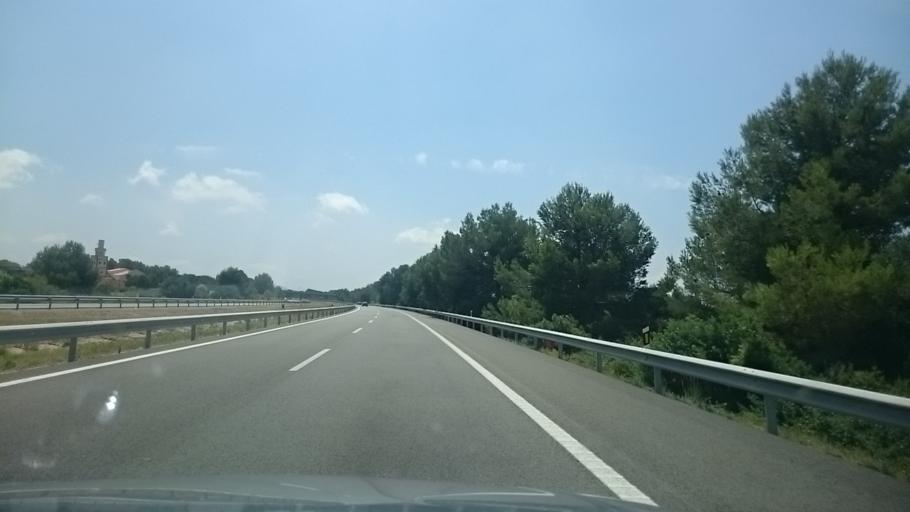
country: ES
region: Catalonia
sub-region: Provincia de Tarragona
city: Alio
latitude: 41.3312
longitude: 1.3232
